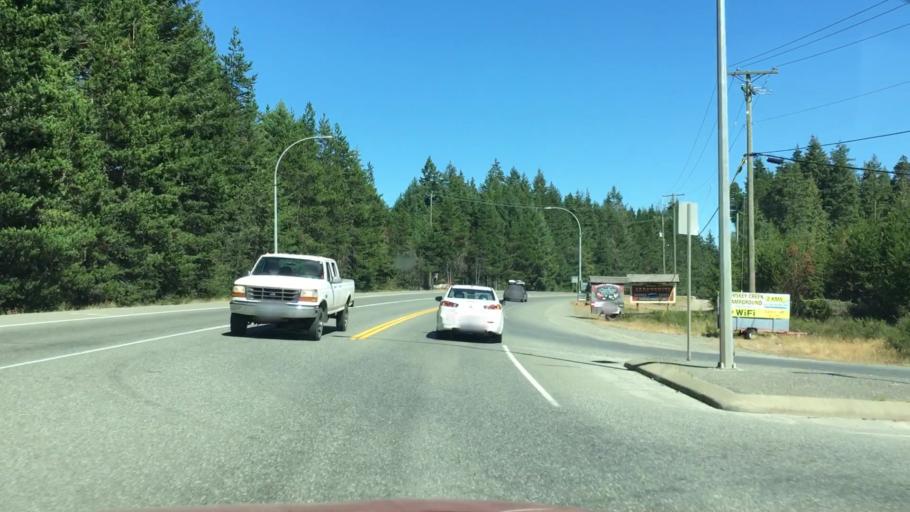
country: CA
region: British Columbia
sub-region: Regional District of Nanaimo
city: Parksville
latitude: 49.3111
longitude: -124.5301
